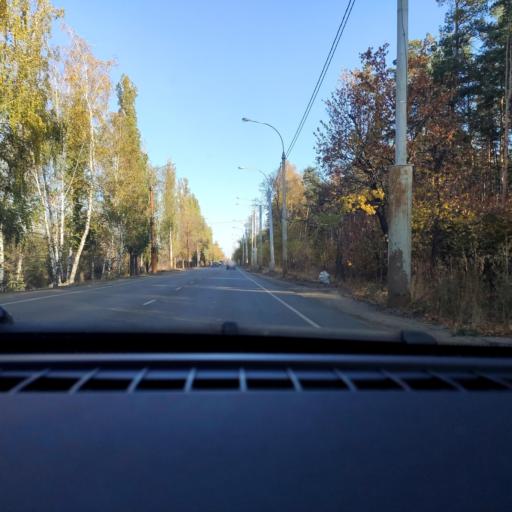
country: RU
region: Voronezj
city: Somovo
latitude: 51.7068
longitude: 39.2915
